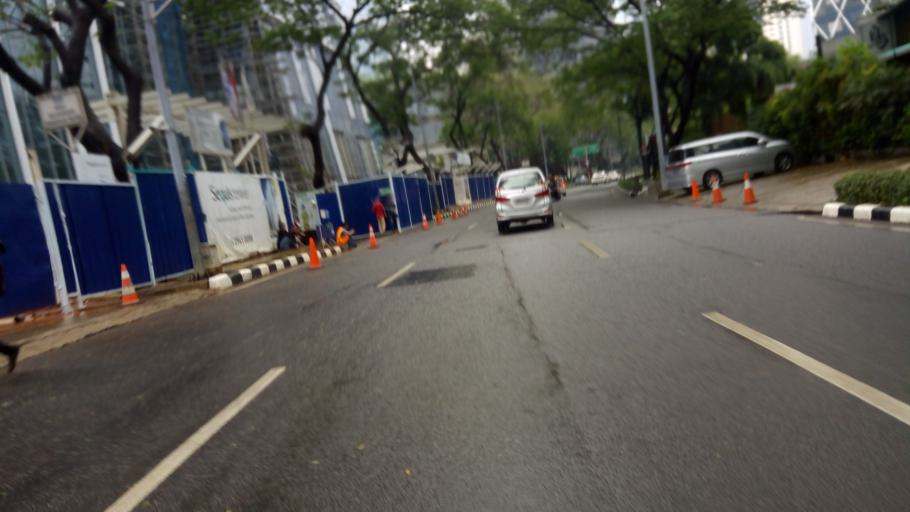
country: ID
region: Jakarta Raya
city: Jakarta
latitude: -6.2262
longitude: 106.8084
